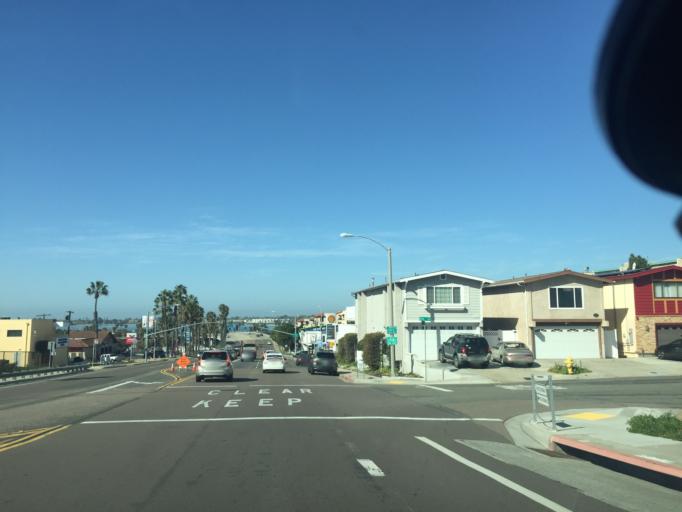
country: US
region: California
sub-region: San Diego County
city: San Diego
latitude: 32.7903
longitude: -117.2020
